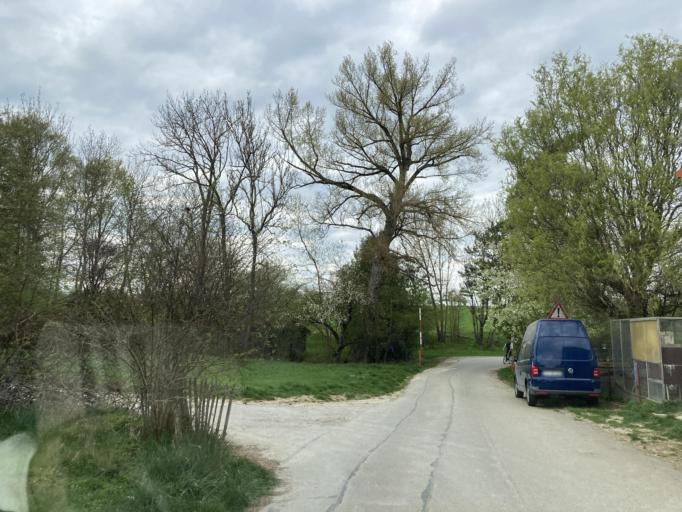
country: DE
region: Baden-Wuerttemberg
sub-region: Tuebingen Region
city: Kusterdingen
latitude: 48.5048
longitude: 9.1283
